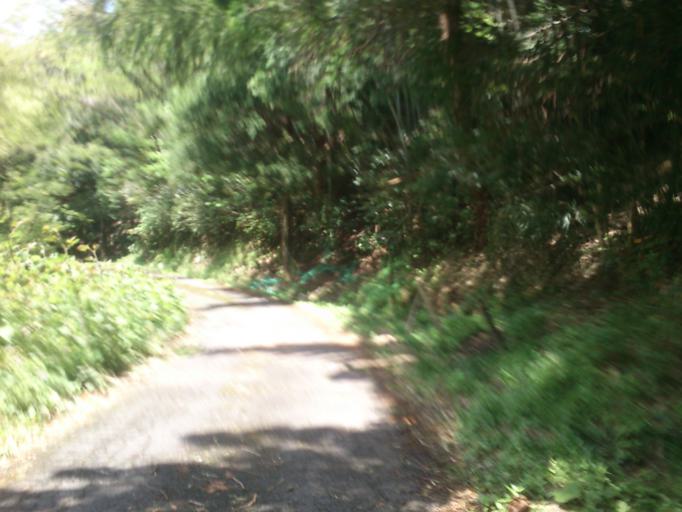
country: JP
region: Kyoto
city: Miyazu
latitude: 35.7027
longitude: 135.1192
